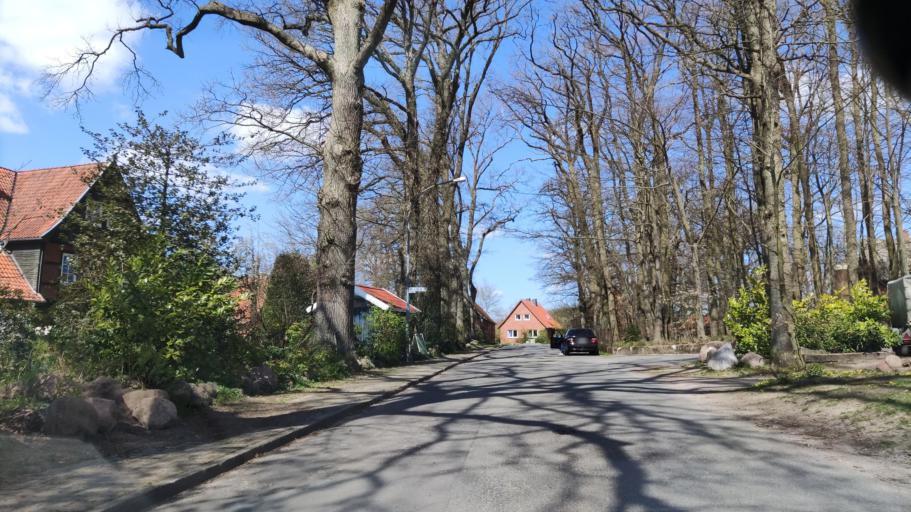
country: DE
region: Lower Saxony
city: Natendorf
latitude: 53.0567
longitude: 10.4838
